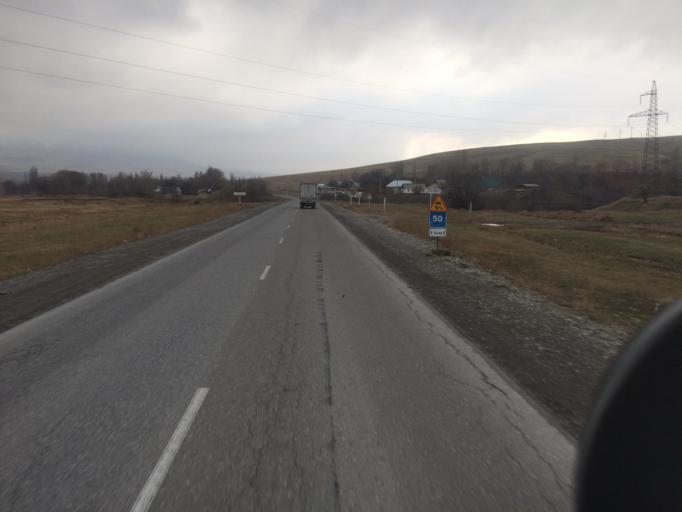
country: KZ
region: Ongtustik Qazaqstan
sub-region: Tulkibas Audany
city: Zhabagly
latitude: 42.5194
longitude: 70.5863
